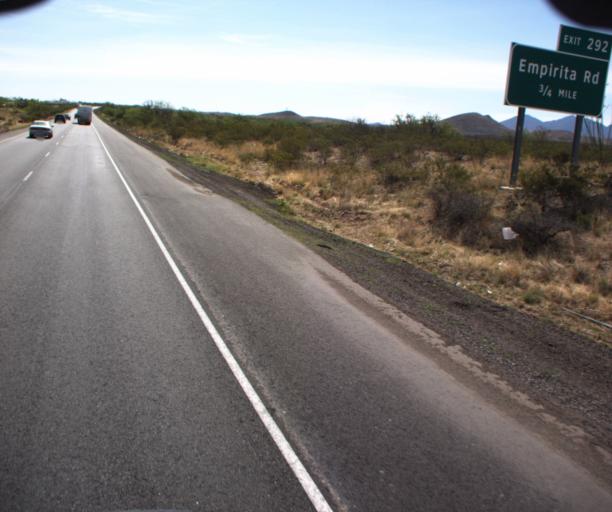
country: US
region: Arizona
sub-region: Cochise County
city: Mescal
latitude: 31.9797
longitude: -110.5242
